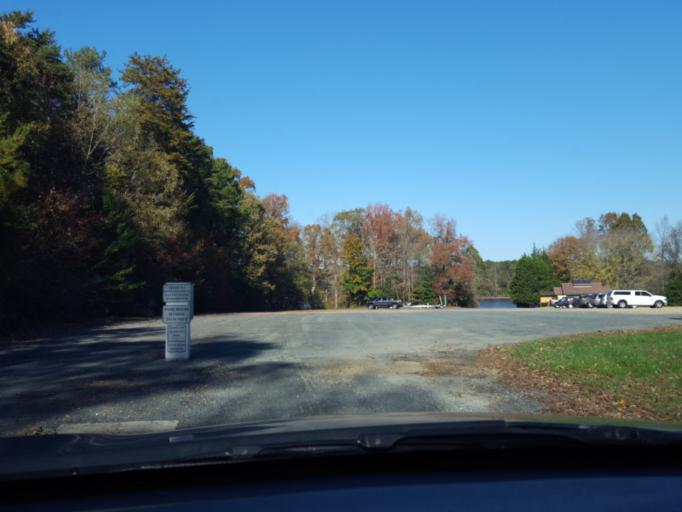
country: US
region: Maryland
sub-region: Saint Mary's County
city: California
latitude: 38.2505
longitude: -76.5420
